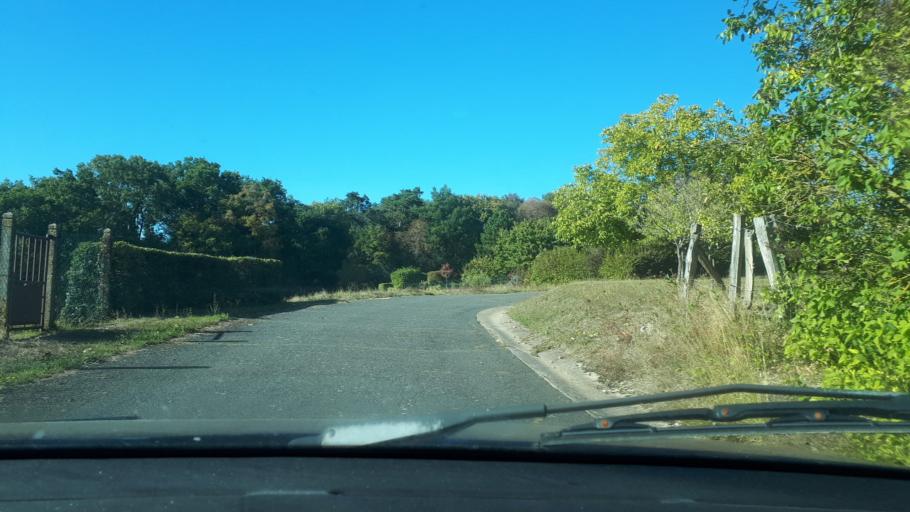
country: FR
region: Centre
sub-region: Departement du Loir-et-Cher
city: Villiers-sur-Loir
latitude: 47.8045
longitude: 0.9999
